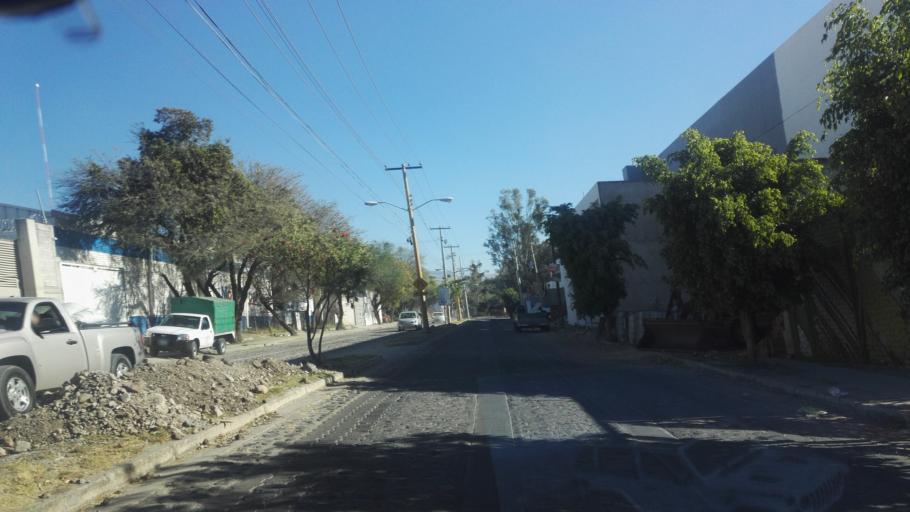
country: MX
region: Guanajuato
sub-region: Leon
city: Fraccionamiento Paraiso Real
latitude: 21.0873
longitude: -101.6116
